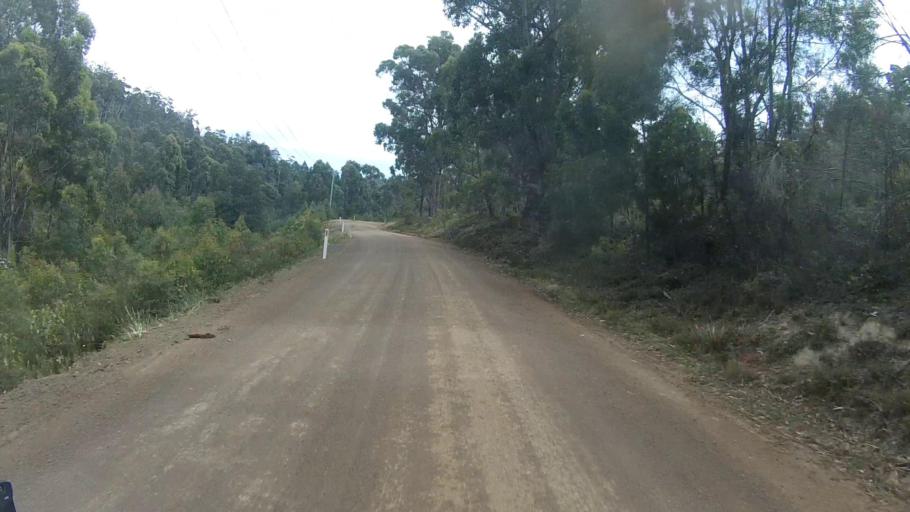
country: AU
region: Tasmania
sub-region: Sorell
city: Sorell
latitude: -42.7629
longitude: 147.8030
